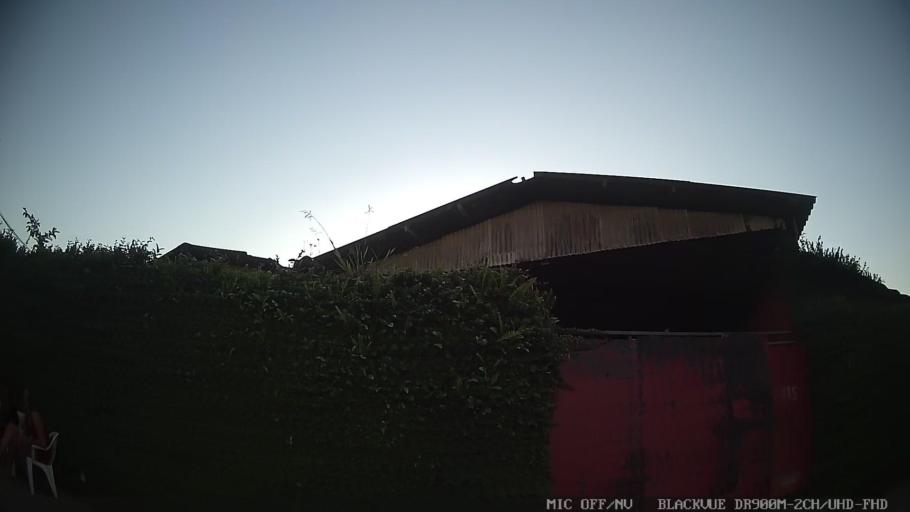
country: BR
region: Sao Paulo
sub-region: Guaruja
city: Guaruja
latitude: -23.9840
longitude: -46.2809
